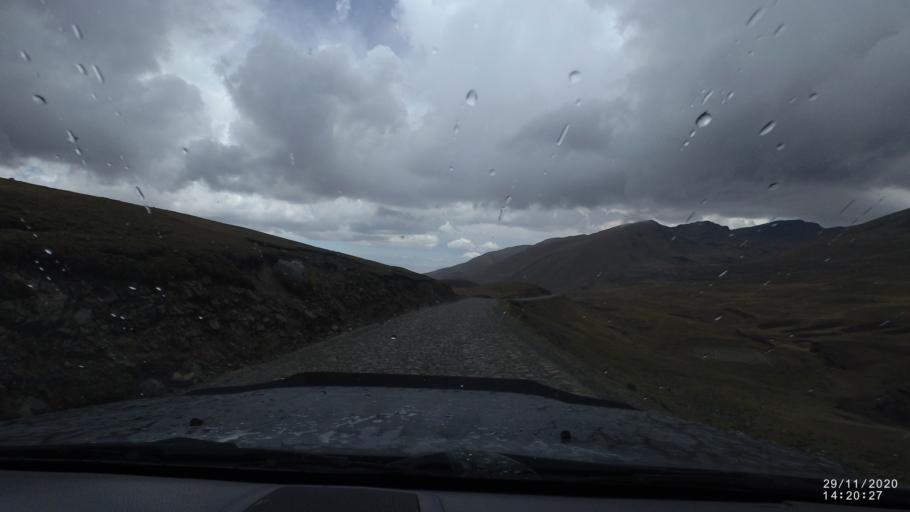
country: BO
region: Cochabamba
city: Sipe Sipe
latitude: -17.2488
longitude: -66.3930
